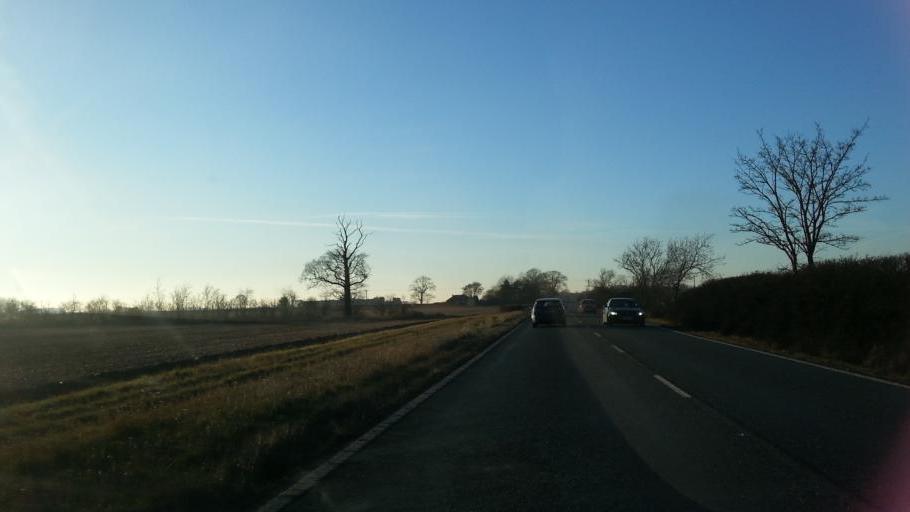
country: GB
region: England
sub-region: Lincolnshire
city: Long Bennington
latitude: 53.0695
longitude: -0.6525
